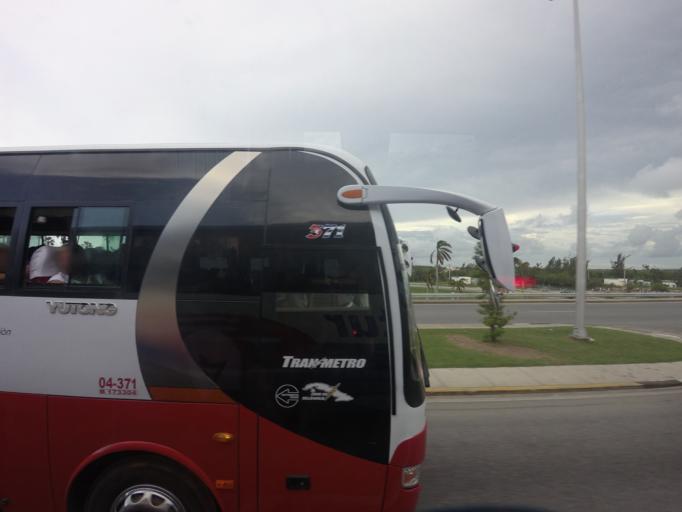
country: CU
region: Matanzas
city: Varadero
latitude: 23.1341
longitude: -81.2823
